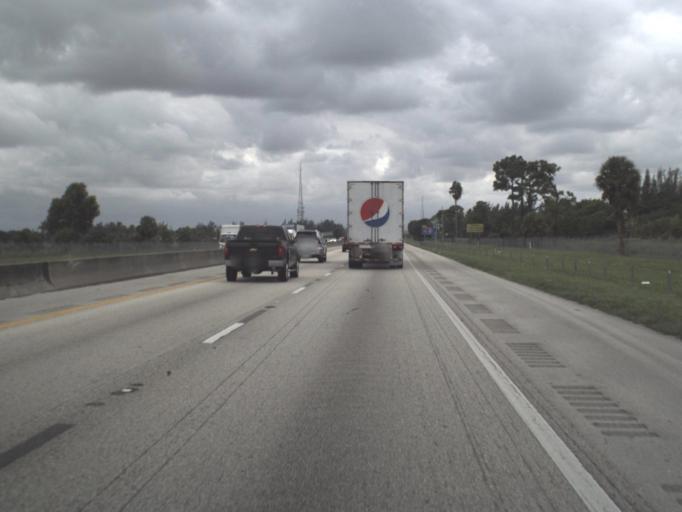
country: US
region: Florida
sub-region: Palm Beach County
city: Lake Belvedere Estates
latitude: 26.6607
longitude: -80.1744
